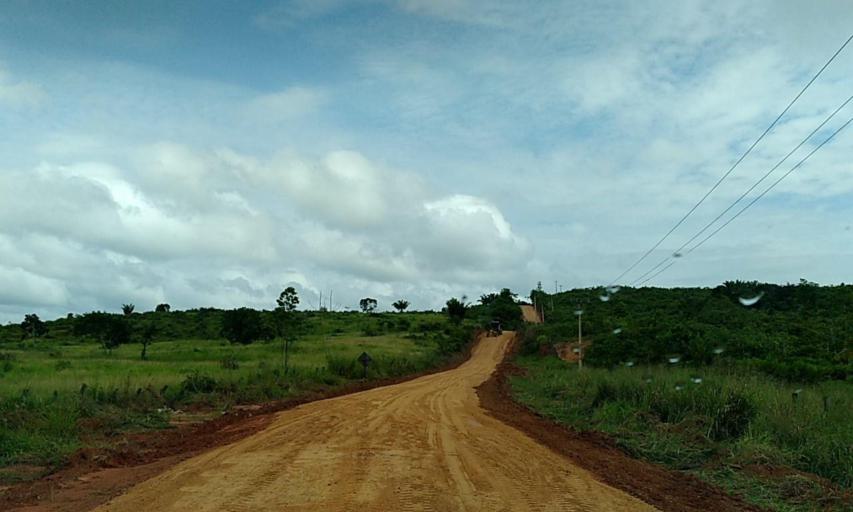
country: BR
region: Para
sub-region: Altamira
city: Altamira
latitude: -3.0858
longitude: -51.6345
